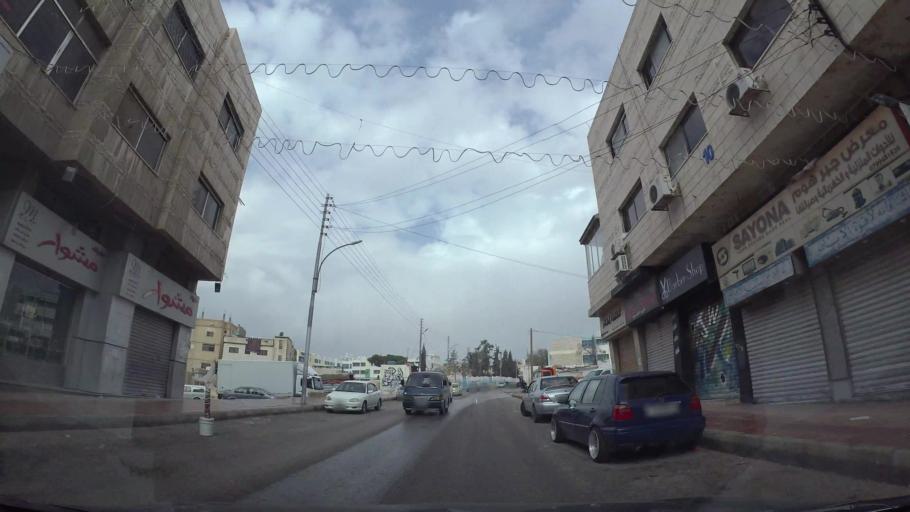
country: JO
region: Amman
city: Amman
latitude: 31.9723
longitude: 35.9279
